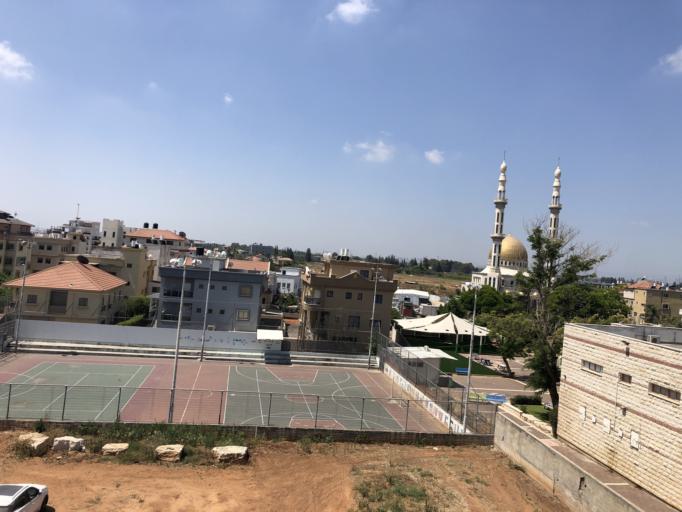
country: IL
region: Central District
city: Jaljulya
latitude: 32.1520
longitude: 34.9548
